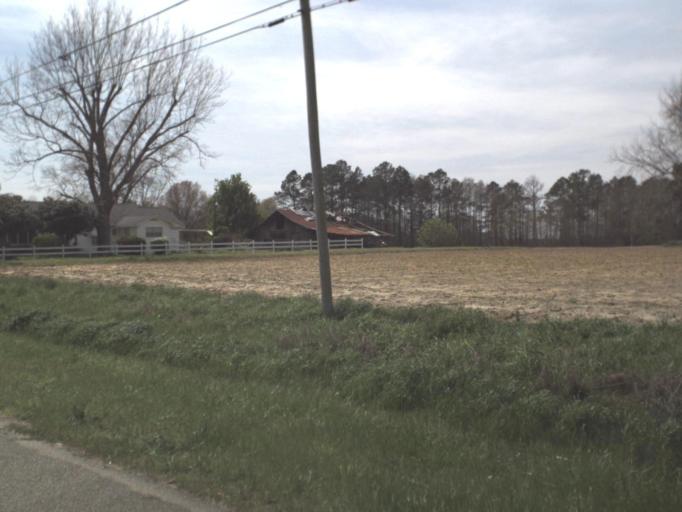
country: US
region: Florida
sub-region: Washington County
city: Chipley
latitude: 30.8425
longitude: -85.5314
